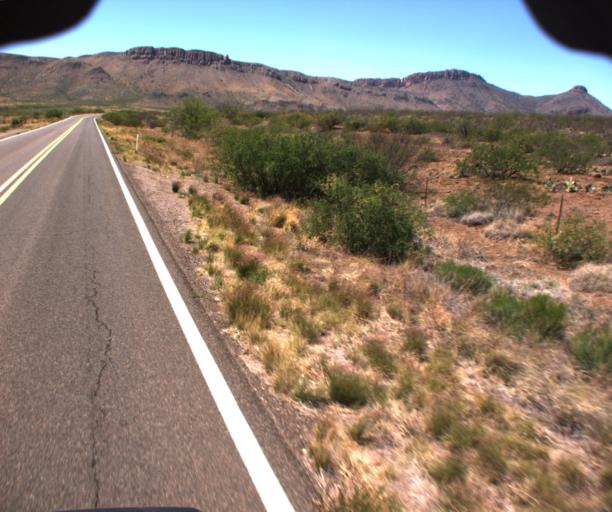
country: US
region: Arizona
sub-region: Cochise County
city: Douglas
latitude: 31.4628
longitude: -109.3646
